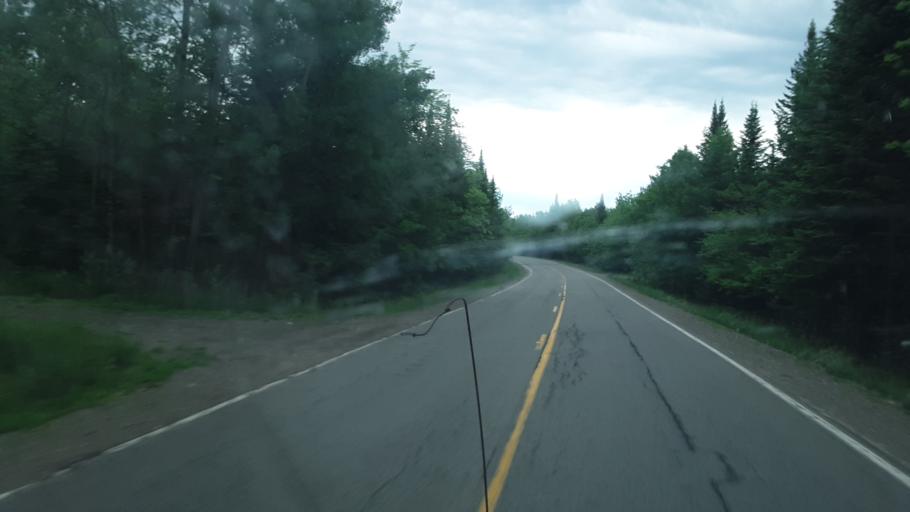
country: US
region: Maine
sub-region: Penobscot County
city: Medway
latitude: 45.7564
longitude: -68.3127
